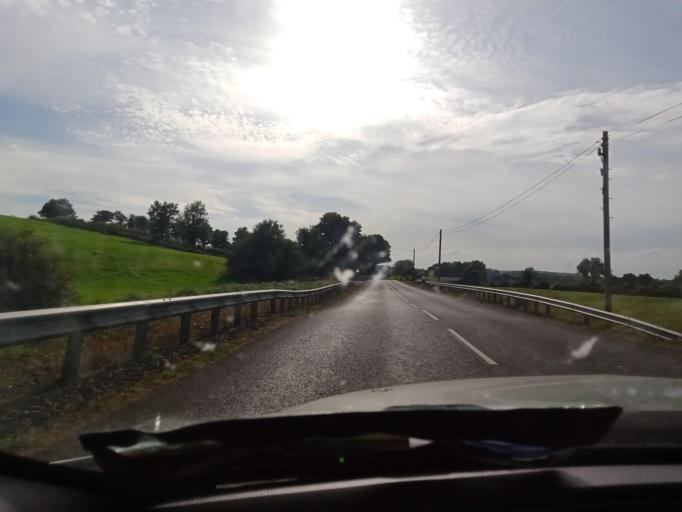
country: IE
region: Leinster
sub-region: An Longfort
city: Granard
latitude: 53.8309
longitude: -7.4307
